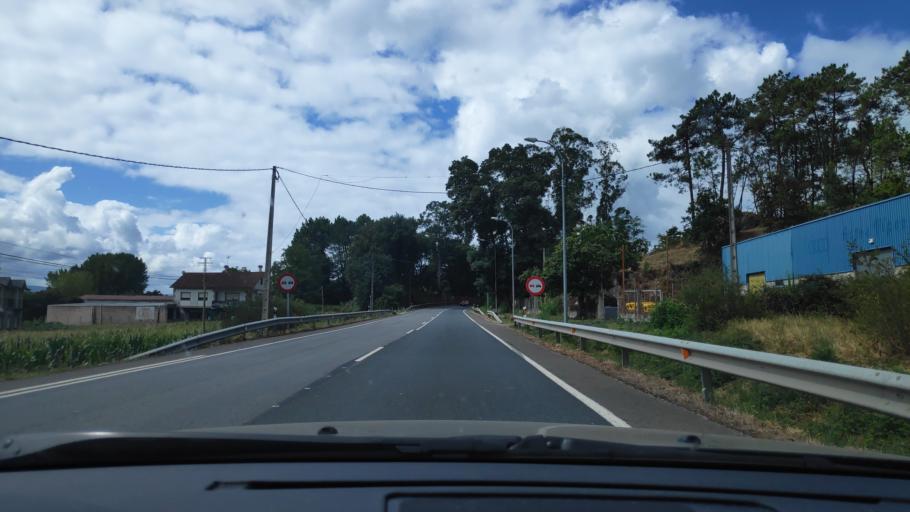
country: ES
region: Galicia
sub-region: Provincia de Pontevedra
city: Portas
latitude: 42.5819
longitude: -8.6985
